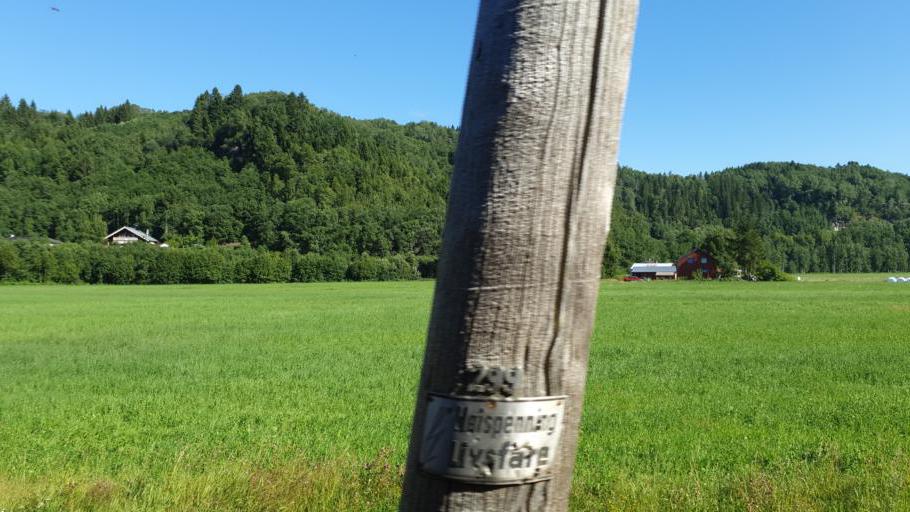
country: NO
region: Sor-Trondelag
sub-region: Orkdal
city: Orkanger
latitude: 63.2088
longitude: 9.7868
